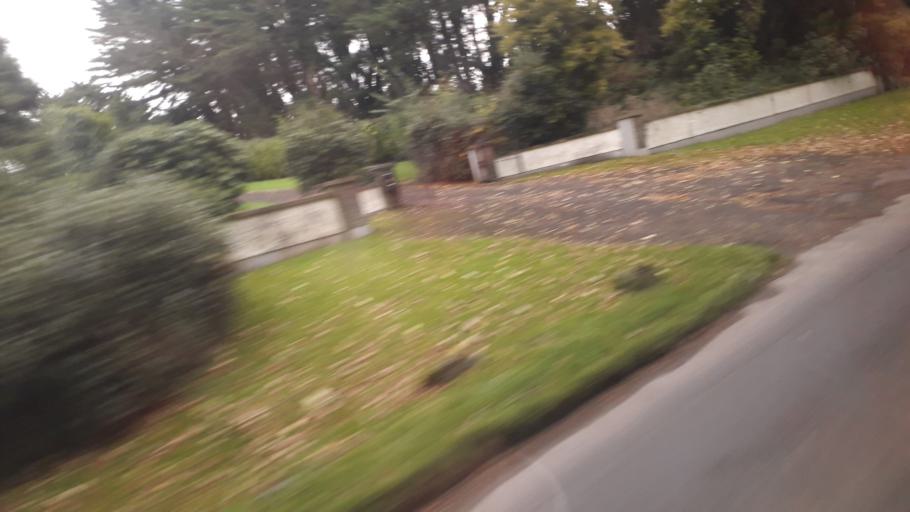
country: IE
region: Munster
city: Ballina
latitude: 52.7954
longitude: -8.4347
